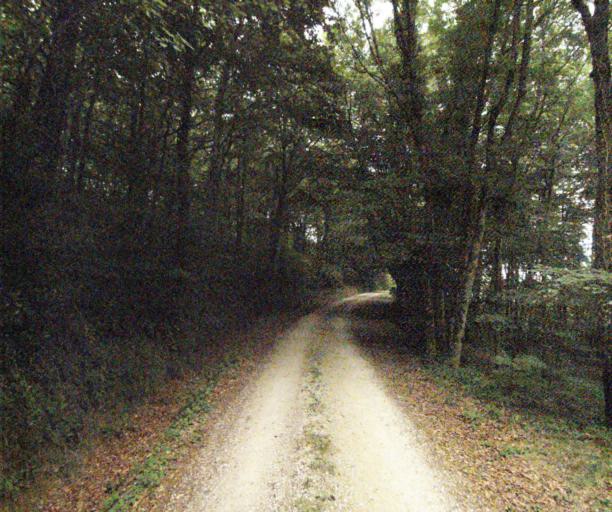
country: FR
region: Midi-Pyrenees
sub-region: Departement du Tarn
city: Soreze
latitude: 43.4304
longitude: 2.0920
